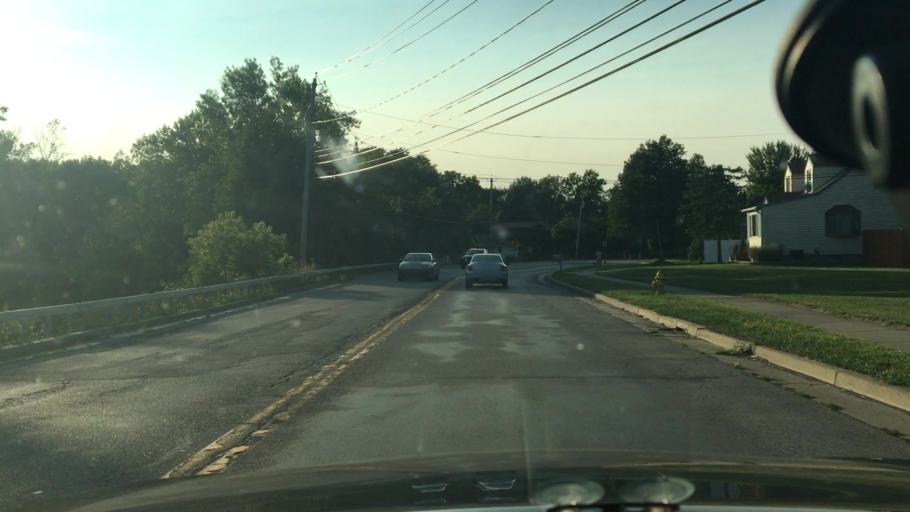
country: US
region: New York
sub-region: Erie County
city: Amherst
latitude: 43.0039
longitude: -78.7619
